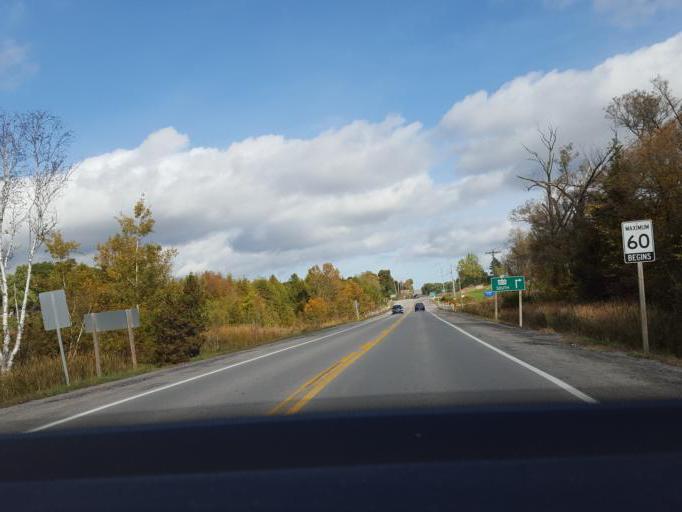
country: CA
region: Ontario
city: Oshawa
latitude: 43.9919
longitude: -78.6167
